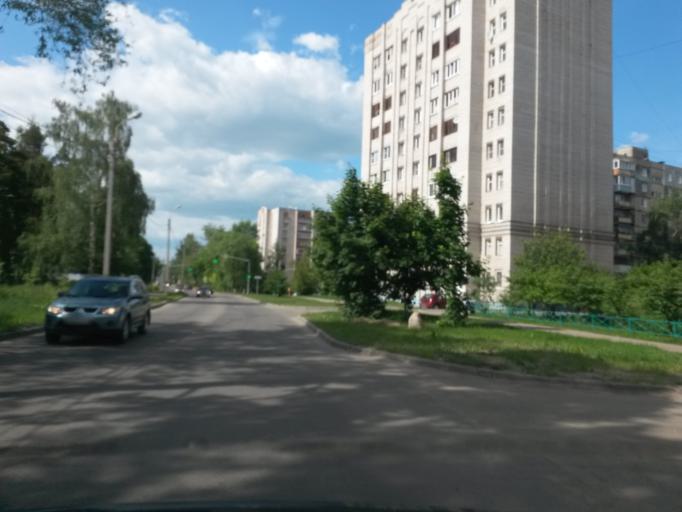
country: RU
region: Jaroslavl
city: Yaroslavl
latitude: 57.6461
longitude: 39.9405
